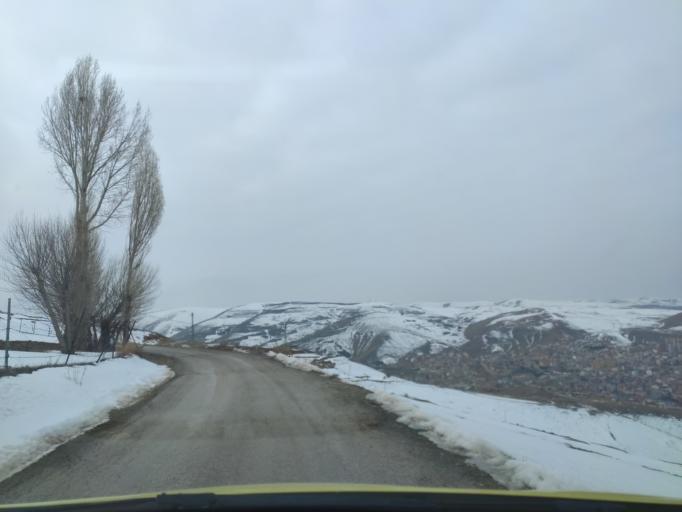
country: TR
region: Bayburt
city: Bayburt
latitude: 40.2625
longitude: 40.2437
